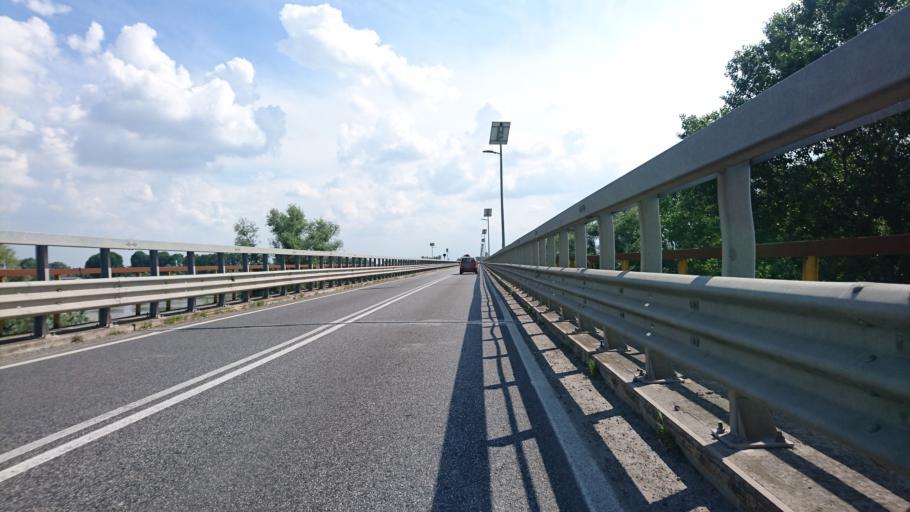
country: IT
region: Veneto
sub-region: Provincia di Rovigo
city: Castelnovo Bariano
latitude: 45.0181
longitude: 11.2911
